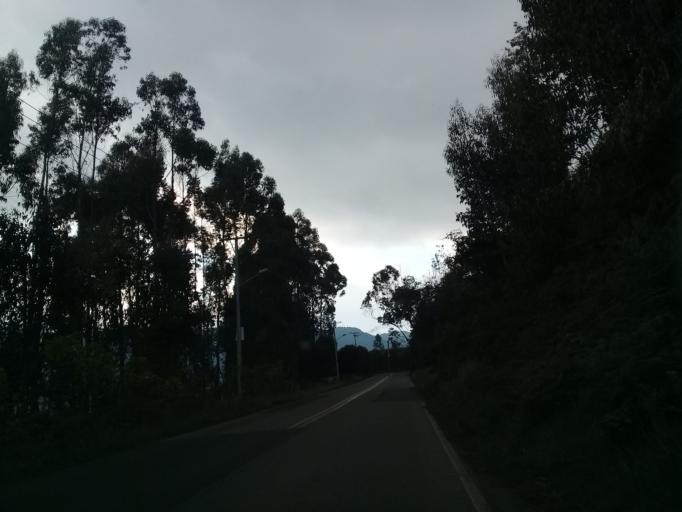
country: CO
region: Cundinamarca
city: Zipaquira
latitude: 5.0493
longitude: -74.0544
